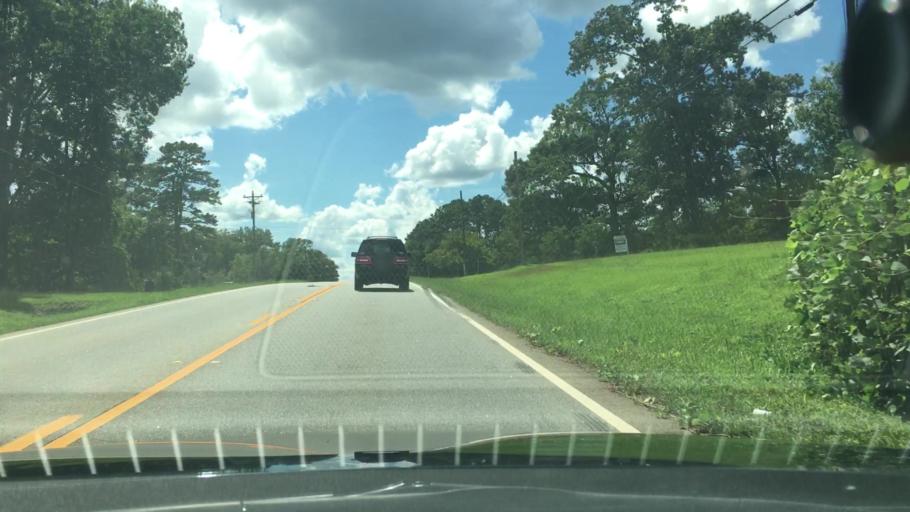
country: US
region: Georgia
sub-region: Putnam County
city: Eatonton
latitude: 33.3185
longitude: -83.4167
